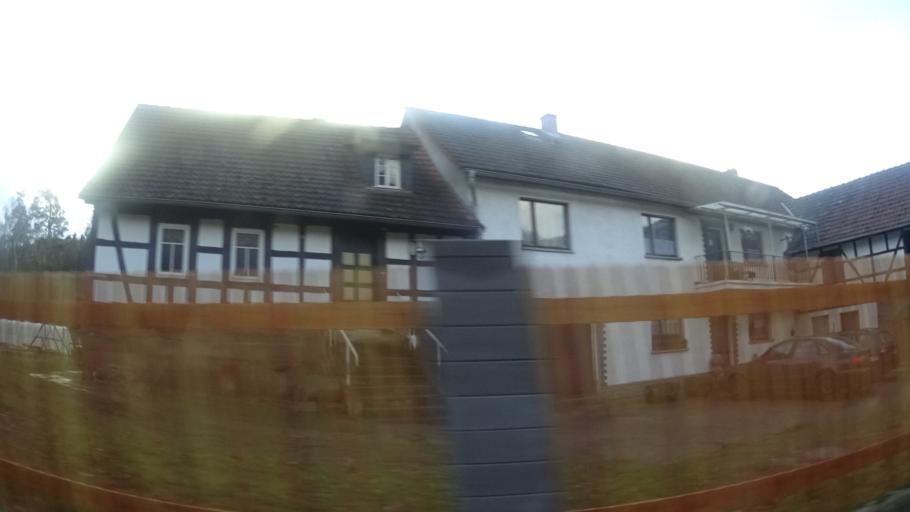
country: DE
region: Thuringia
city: Unterwellenborn
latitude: 50.6902
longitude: 11.4114
